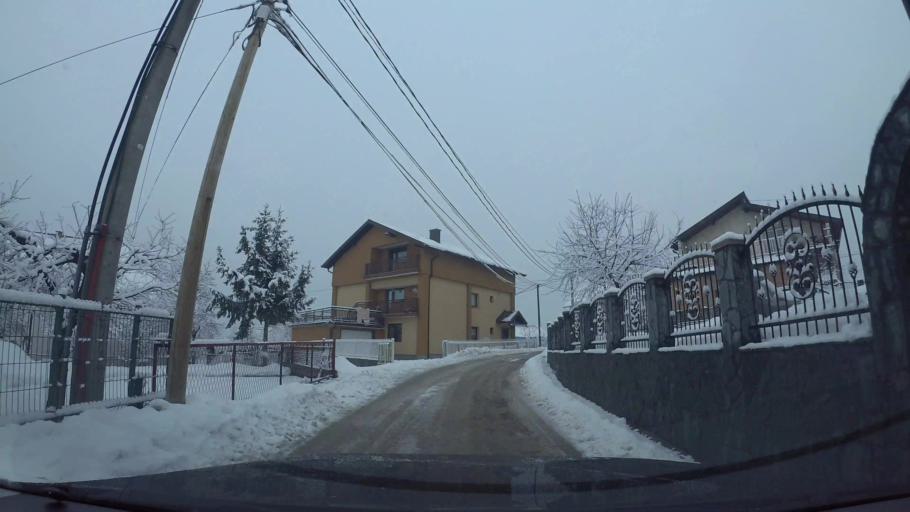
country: BA
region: Federation of Bosnia and Herzegovina
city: Vogosca
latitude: 43.8697
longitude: 18.3183
